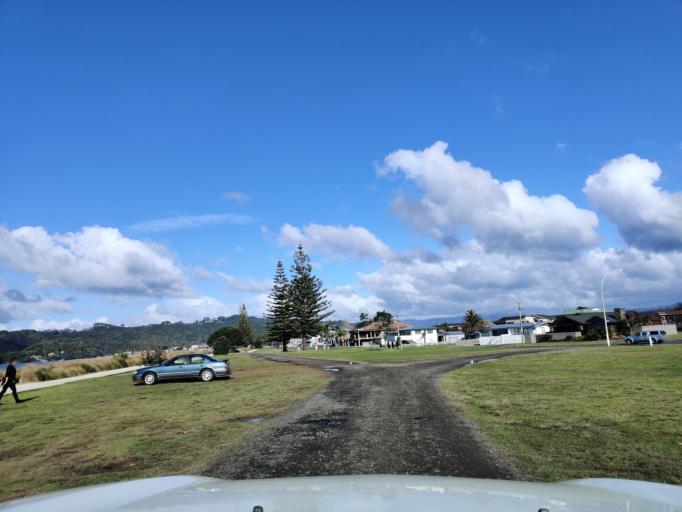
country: NZ
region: Waikato
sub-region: Thames-Coromandel District
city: Whitianga
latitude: -36.8227
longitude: 175.7017
